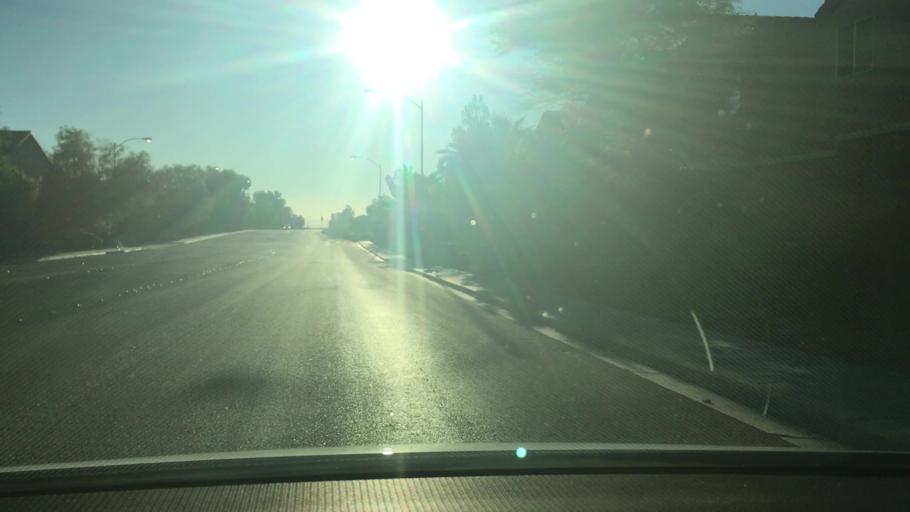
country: US
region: Nevada
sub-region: Clark County
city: Summerlin South
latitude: 36.0776
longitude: -115.3059
